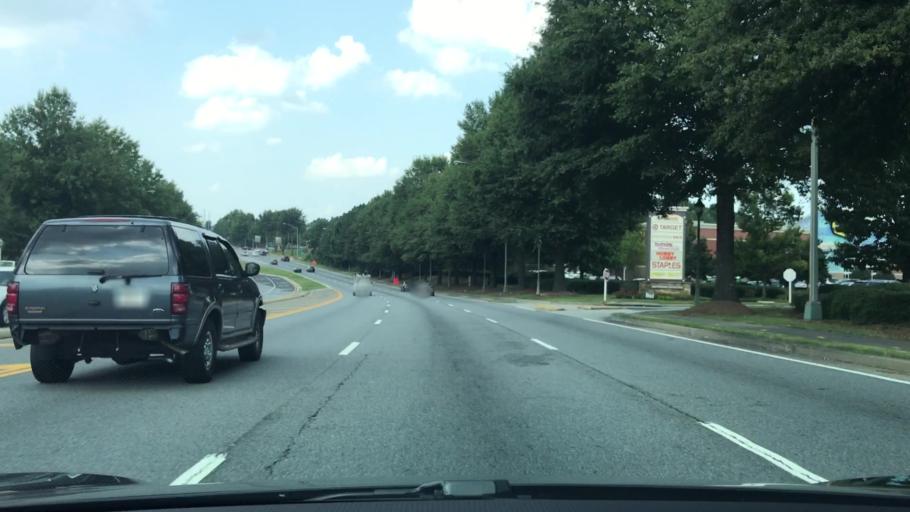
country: US
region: Georgia
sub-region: Gwinnett County
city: Buford
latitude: 34.0695
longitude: -83.9850
